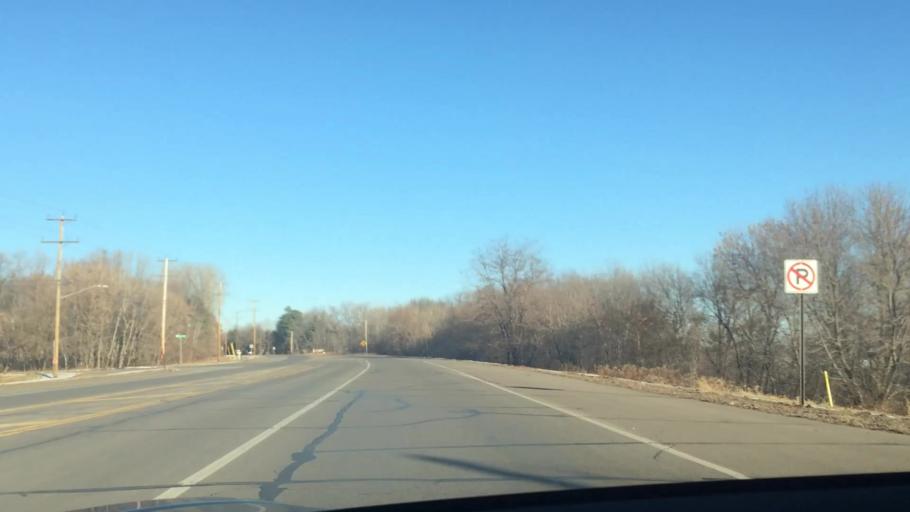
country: US
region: Minnesota
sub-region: Anoka County
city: Circle Pines
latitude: 45.1547
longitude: -93.1328
